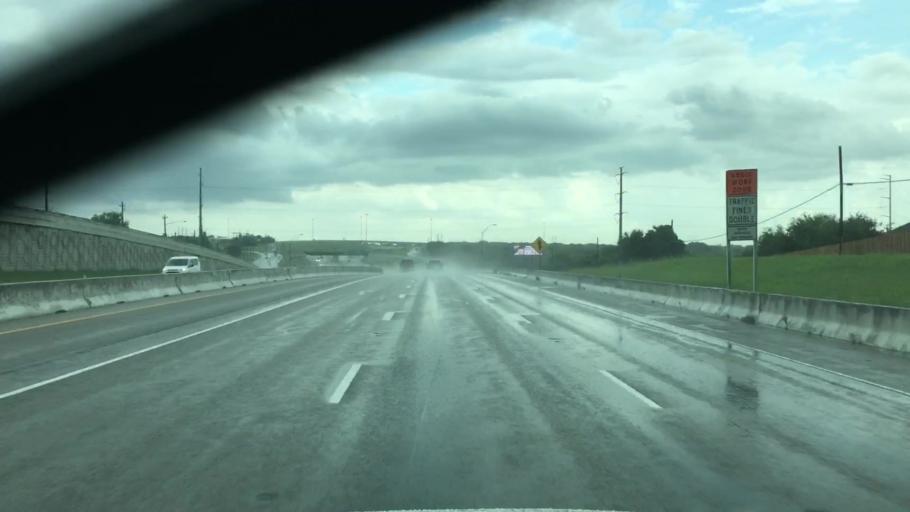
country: US
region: Texas
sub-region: Nueces County
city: Robstown
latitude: 27.8599
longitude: -97.6100
